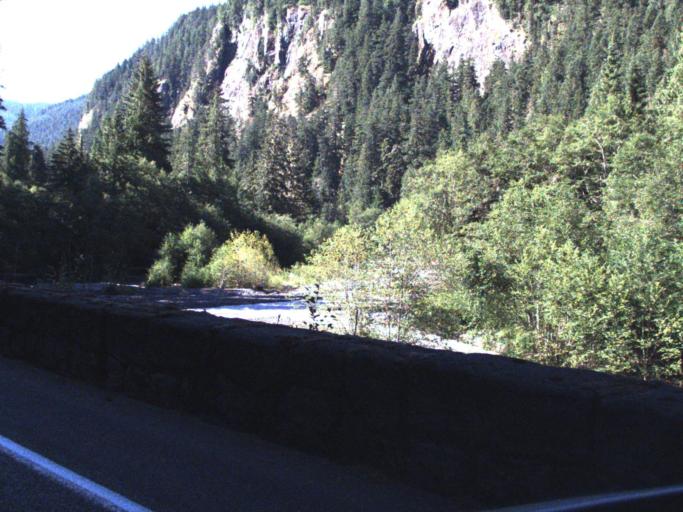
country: US
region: Washington
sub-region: King County
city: Enumclaw
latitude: 47.0601
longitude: -121.5747
